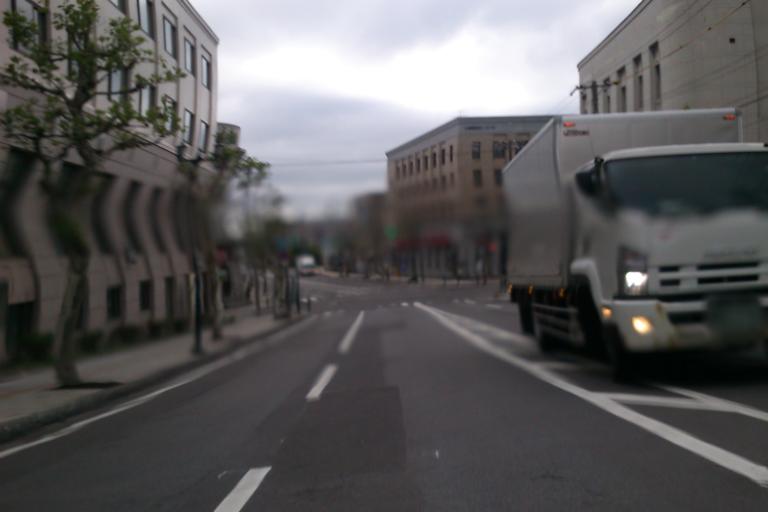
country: JP
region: Hokkaido
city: Otaru
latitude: 43.1966
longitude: 141.0008
